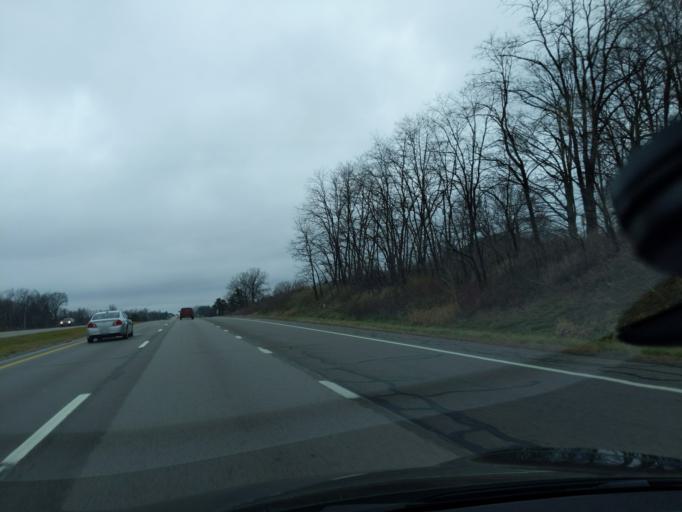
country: US
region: Michigan
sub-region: Ingham County
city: Leslie
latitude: 42.4557
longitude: -84.4434
